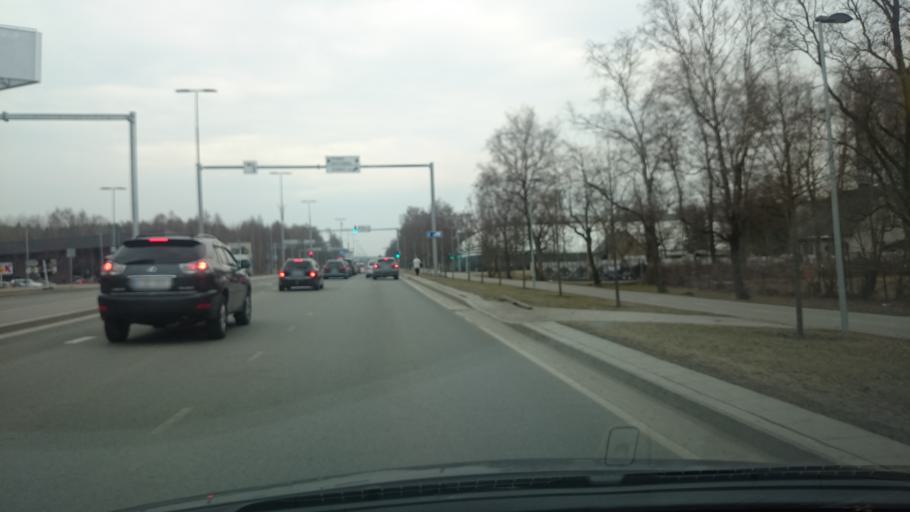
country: EE
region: Harju
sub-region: Saue vald
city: Laagri
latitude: 59.4219
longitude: 24.6484
